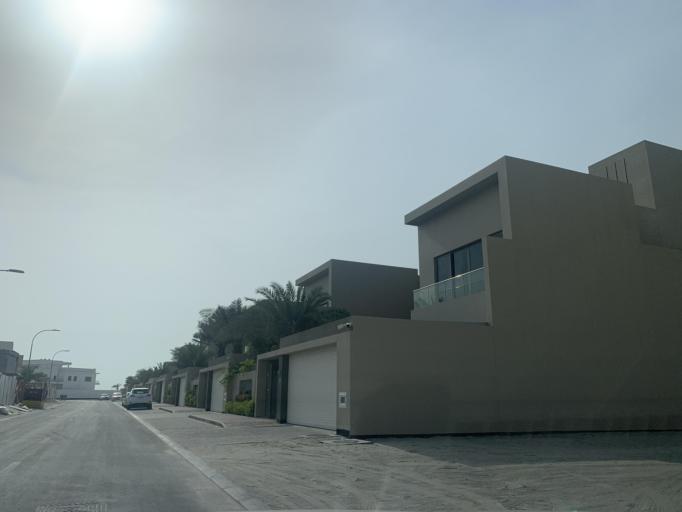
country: BH
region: Muharraq
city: Al Muharraq
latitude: 26.3235
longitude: 50.6272
